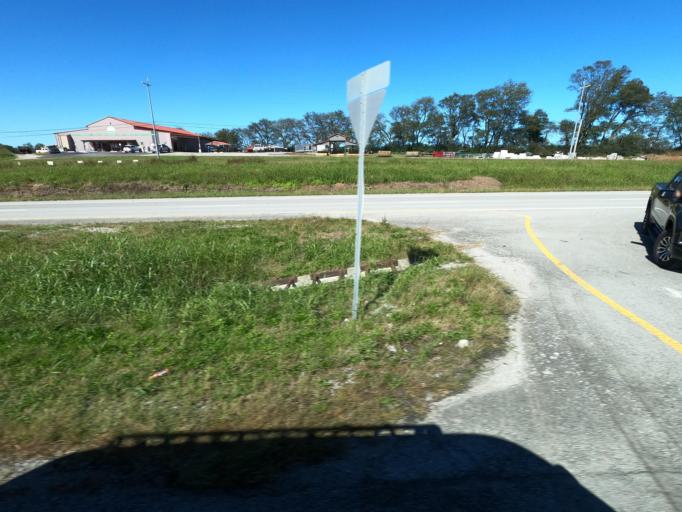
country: US
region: Tennessee
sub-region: Maury County
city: Mount Pleasant
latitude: 35.5571
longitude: -87.1928
